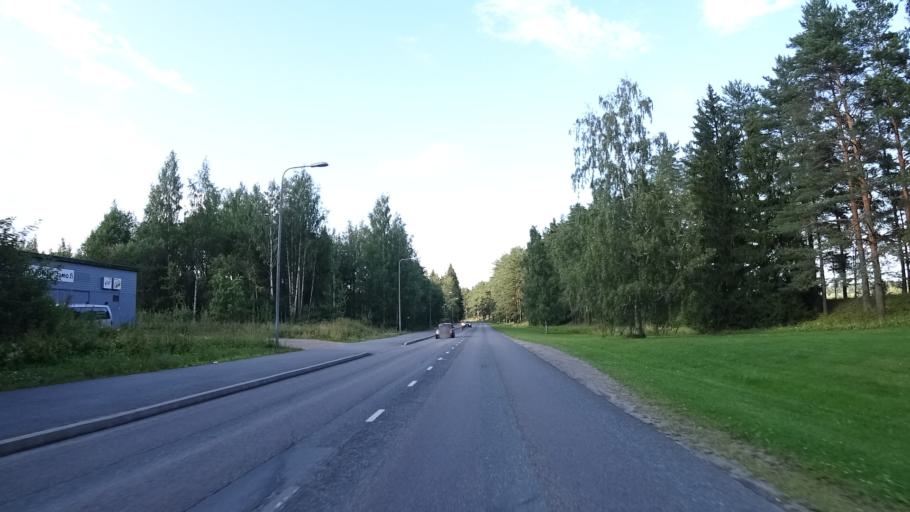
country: FI
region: South Karelia
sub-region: Imatra
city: Imatra
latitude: 61.1767
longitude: 28.7790
